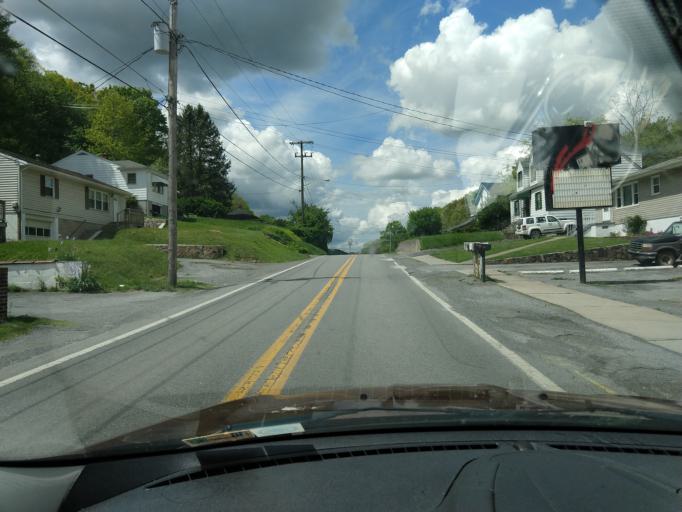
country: US
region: West Virginia
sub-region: Mercer County
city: Bluefield
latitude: 37.2530
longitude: -81.2373
